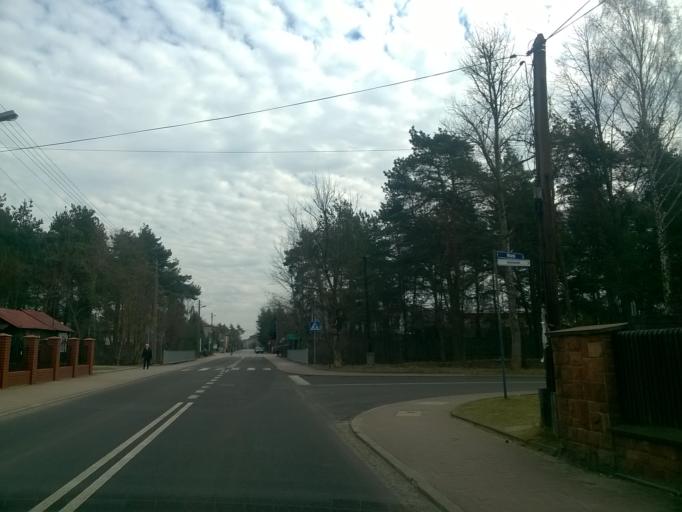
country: PL
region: Lesser Poland Voivodeship
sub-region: Powiat olkuski
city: Bukowno
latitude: 50.2628
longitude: 19.4619
